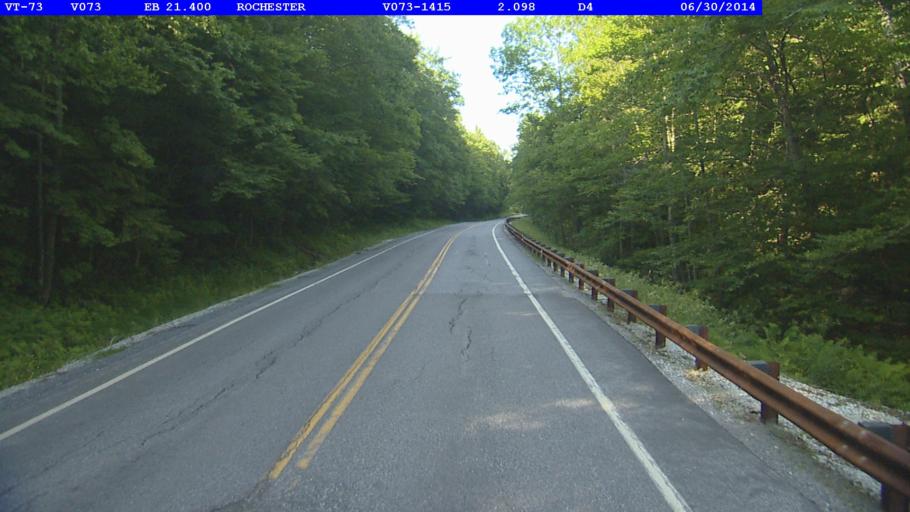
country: US
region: Vermont
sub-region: Rutland County
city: Brandon
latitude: 43.8489
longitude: -72.9268
